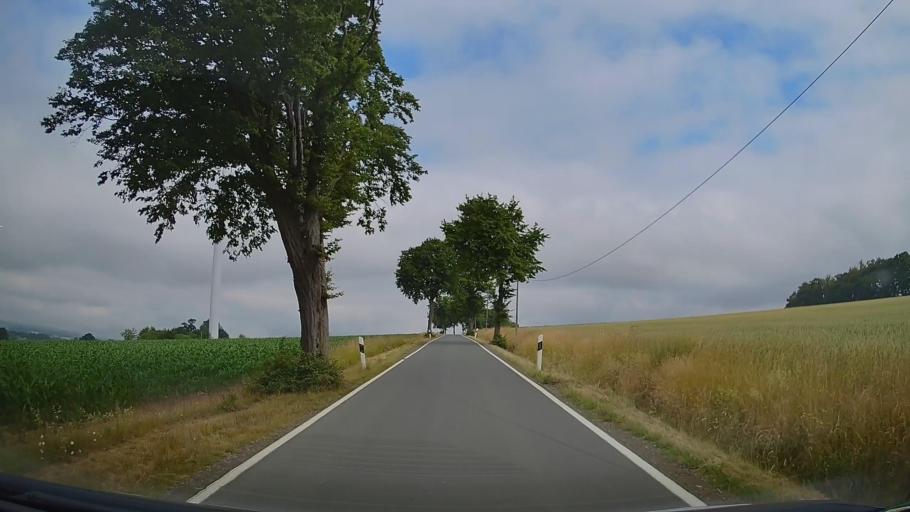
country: DE
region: North Rhine-Westphalia
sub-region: Regierungsbezirk Detmold
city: Barntrup
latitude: 52.0819
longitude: 9.1330
